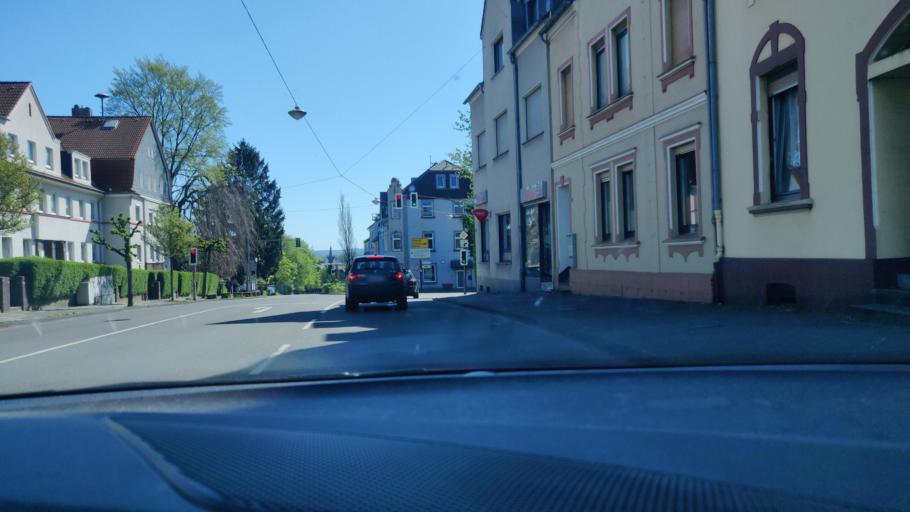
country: DE
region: North Rhine-Westphalia
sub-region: Regierungsbezirk Dusseldorf
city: Mettmann
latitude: 51.2523
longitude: 6.9667
